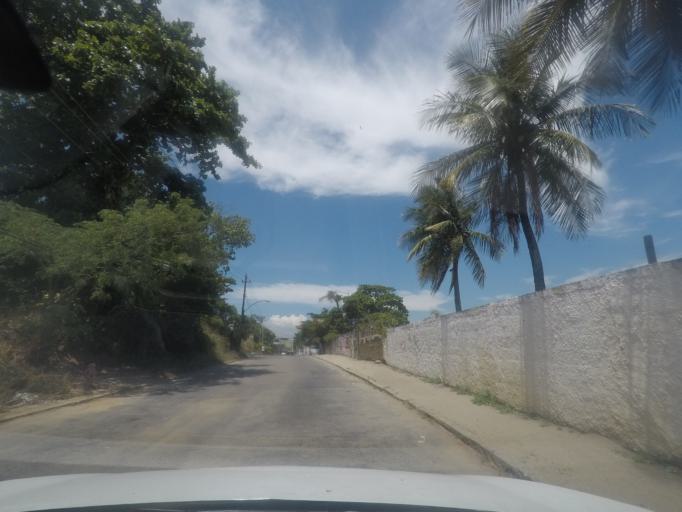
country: BR
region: Rio de Janeiro
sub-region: Itaguai
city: Itaguai
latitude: -22.9853
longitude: -43.6978
